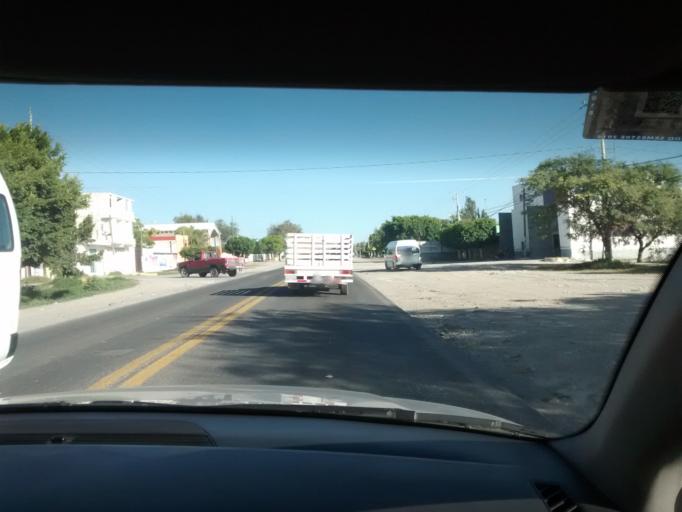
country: MX
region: Puebla
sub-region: Tehuacan
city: Magdalena Cuayucatepec
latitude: 18.5114
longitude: -97.4928
